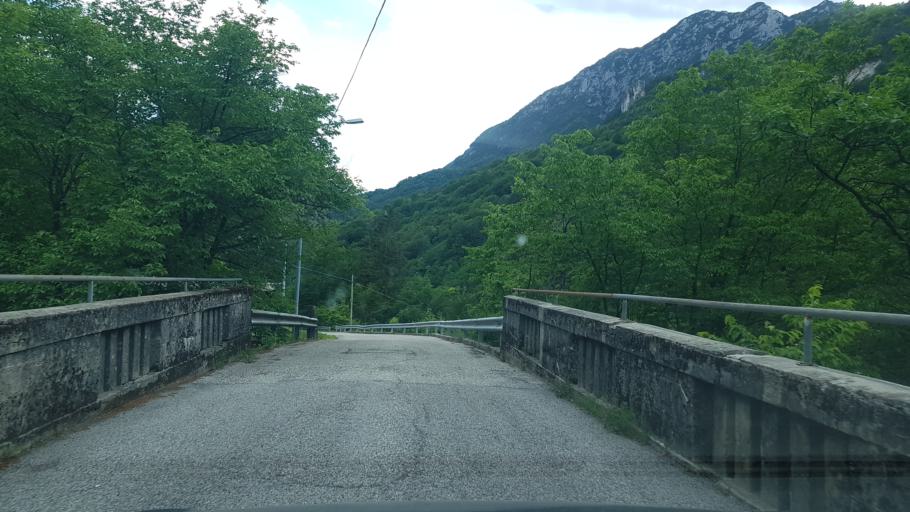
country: IT
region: Friuli Venezia Giulia
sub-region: Provincia di Udine
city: Moggio Udinese
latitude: 46.4654
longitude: 13.1921
